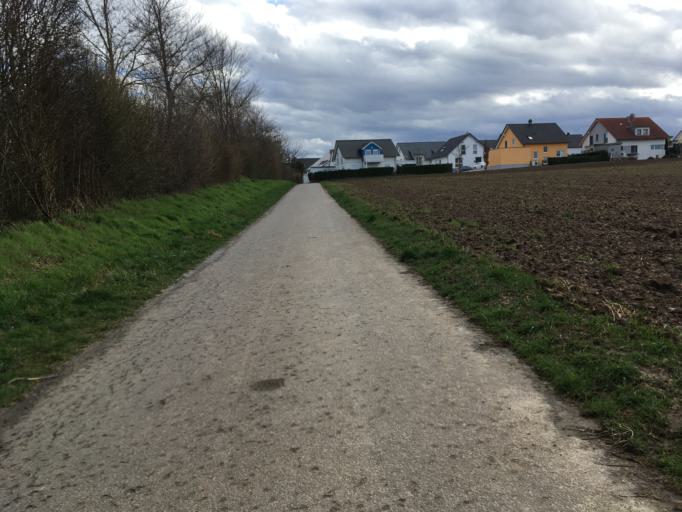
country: DE
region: Baden-Wuerttemberg
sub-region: Regierungsbezirk Stuttgart
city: Ellhofen
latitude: 49.1442
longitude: 9.3146
